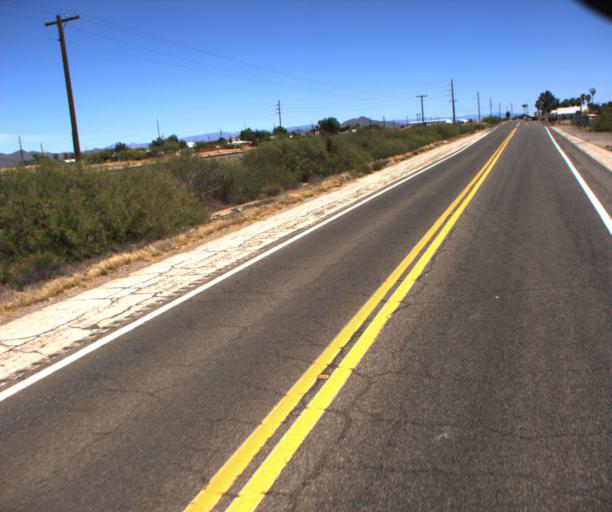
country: US
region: Arizona
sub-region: Yavapai County
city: Congress
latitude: 33.9416
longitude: -113.1811
